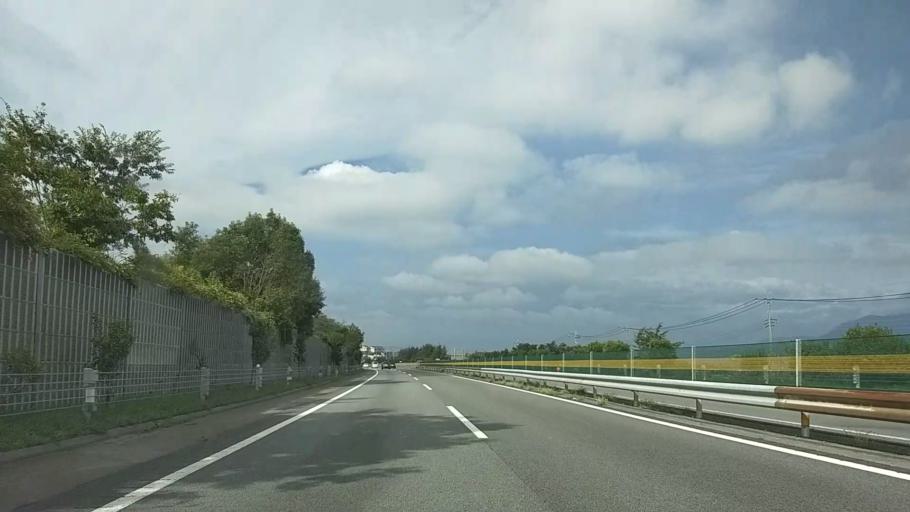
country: JP
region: Yamanashi
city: Isawa
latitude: 35.6381
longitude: 138.6981
